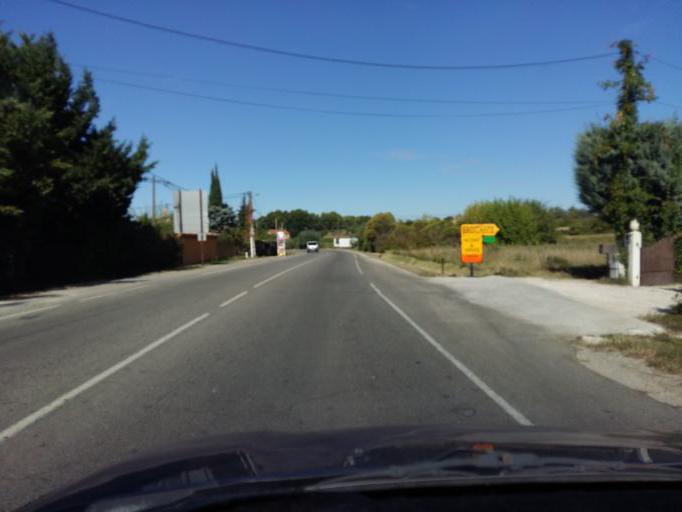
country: FR
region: Provence-Alpes-Cote d'Azur
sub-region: Departement du Vaucluse
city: Mazan
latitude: 44.0583
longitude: 5.1124
